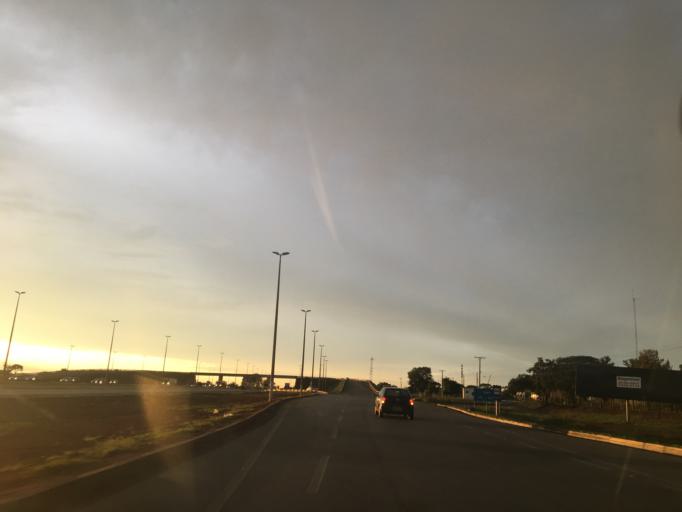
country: BR
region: Federal District
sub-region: Brasilia
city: Brasilia
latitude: -15.9782
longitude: -47.9902
